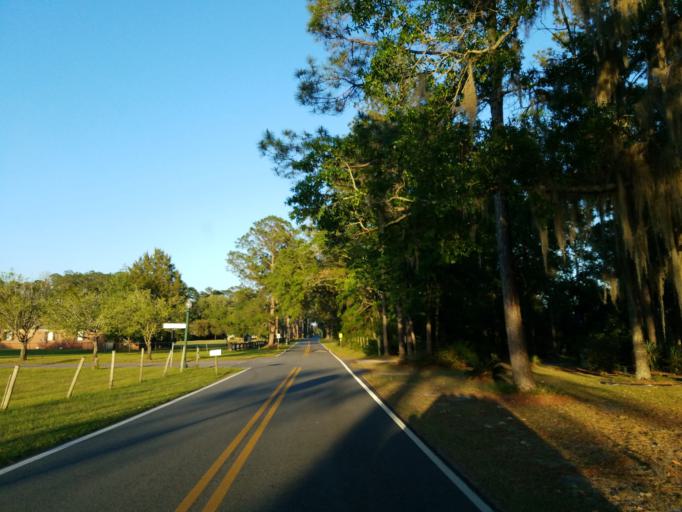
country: US
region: Georgia
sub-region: Lowndes County
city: Valdosta
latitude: 30.7502
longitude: -83.2262
